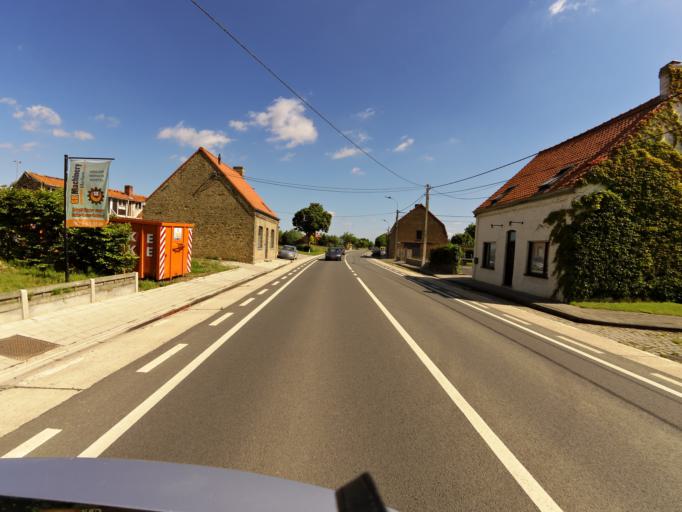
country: BE
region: Flanders
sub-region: Provincie West-Vlaanderen
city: Diksmuide
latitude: 50.9482
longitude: 2.8624
